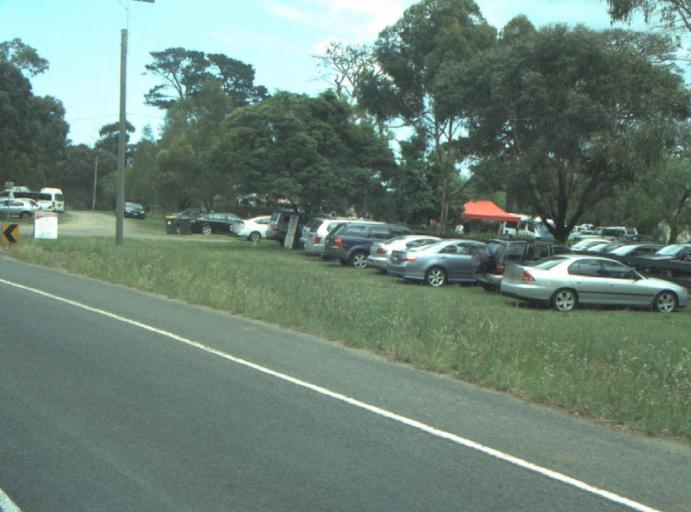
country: AU
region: Victoria
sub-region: Greater Geelong
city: Leopold
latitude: -38.2399
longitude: 144.5015
